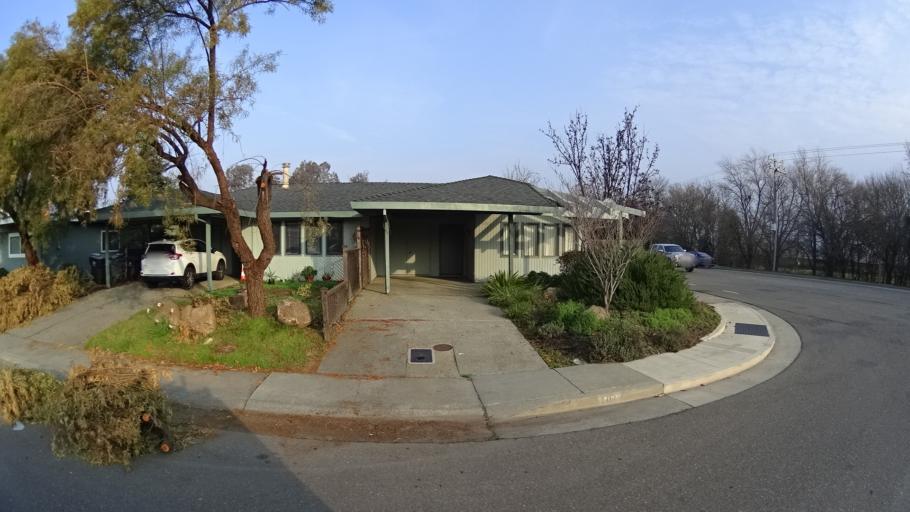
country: US
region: California
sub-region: Yolo County
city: Davis
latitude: 38.5695
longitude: -121.7465
